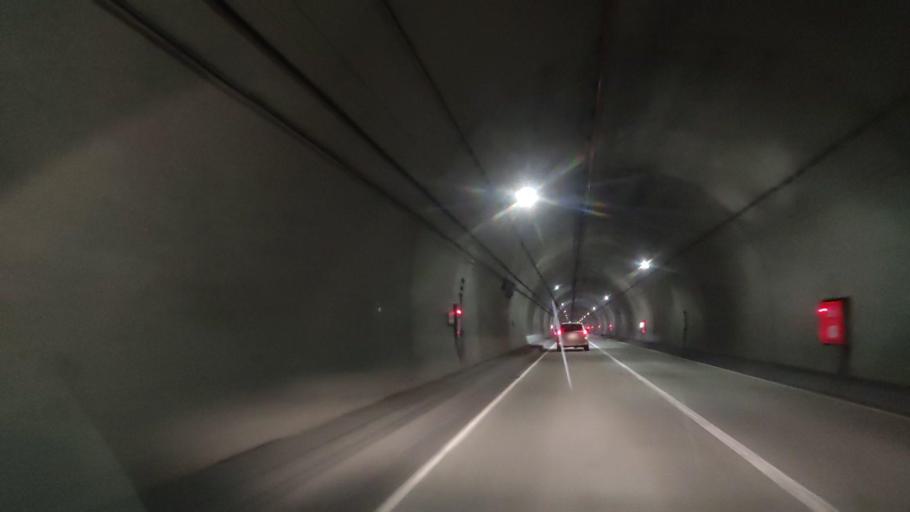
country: JP
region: Hokkaido
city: Rumoi
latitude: 43.7157
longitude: 141.3298
